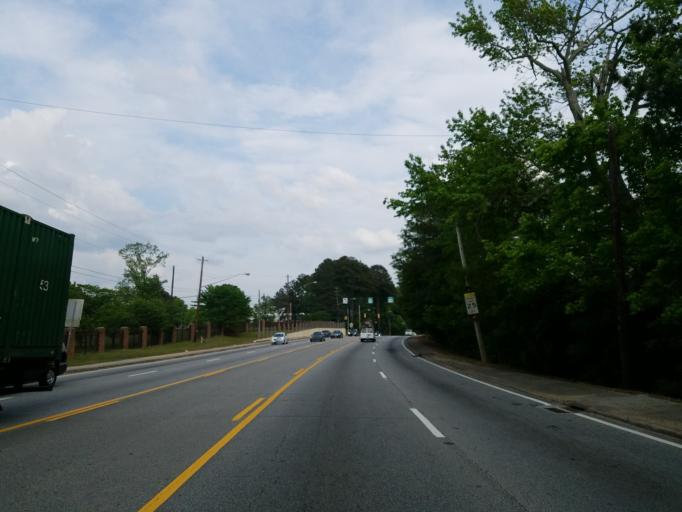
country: US
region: Georgia
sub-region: Cobb County
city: Vinings
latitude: 33.7942
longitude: -84.5020
